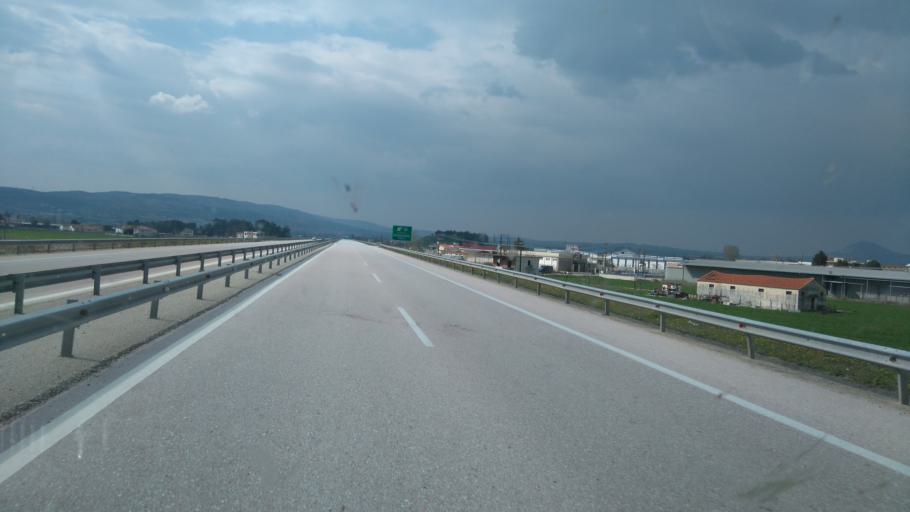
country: GR
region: Central Macedonia
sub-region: Nomos Thessalonikis
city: Kolchikon
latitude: 40.7249
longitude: 23.1106
